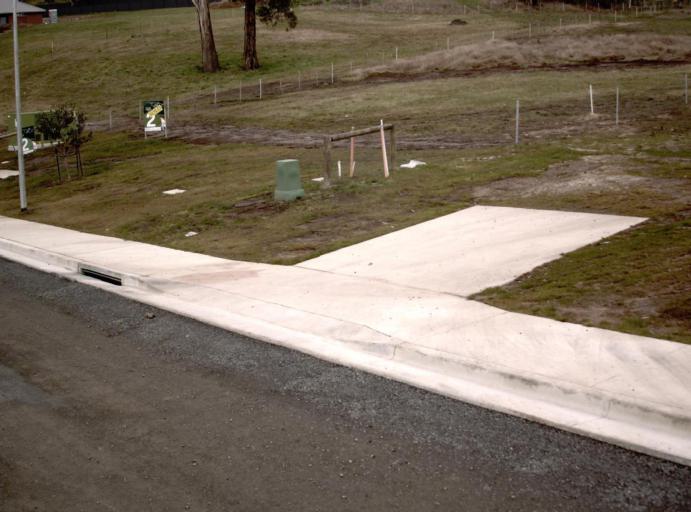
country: AU
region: Tasmania
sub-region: Launceston
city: Newstead
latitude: -41.4763
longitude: 147.1757
